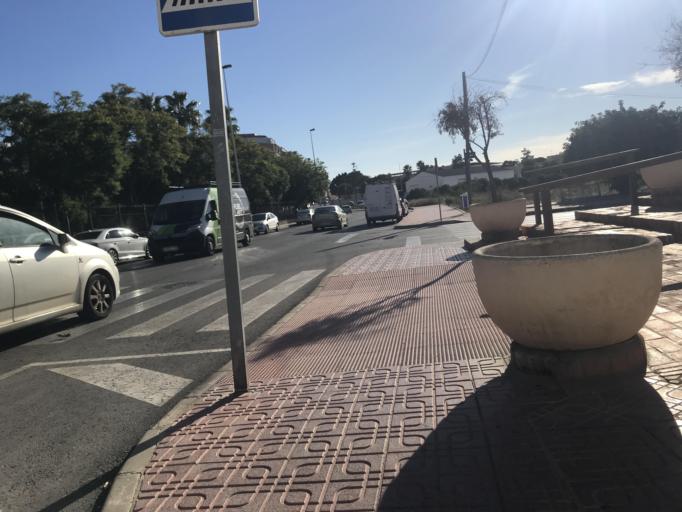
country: ES
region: Valencia
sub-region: Provincia de Alicante
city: Torrevieja
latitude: 37.9790
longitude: -0.6915
